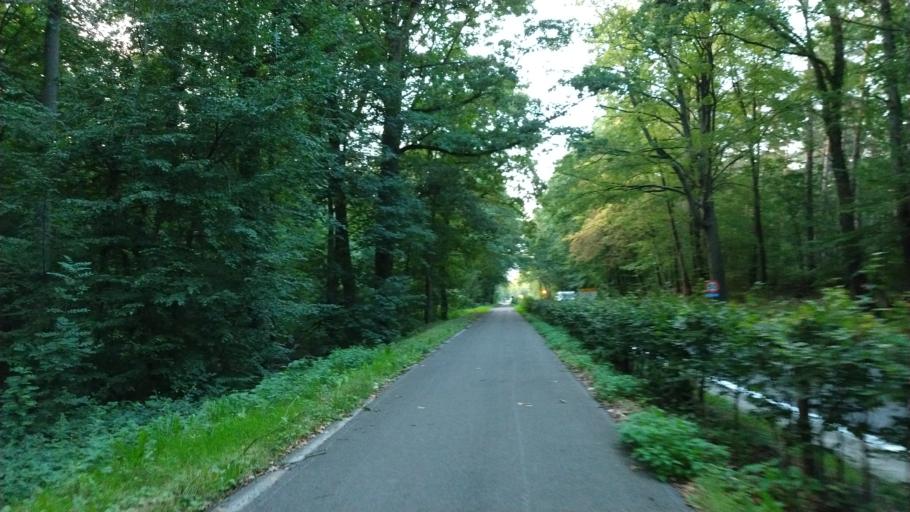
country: BE
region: Flanders
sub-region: Provincie Vlaams-Brabant
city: Oud-Heverlee
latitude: 50.8096
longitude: 4.7062
